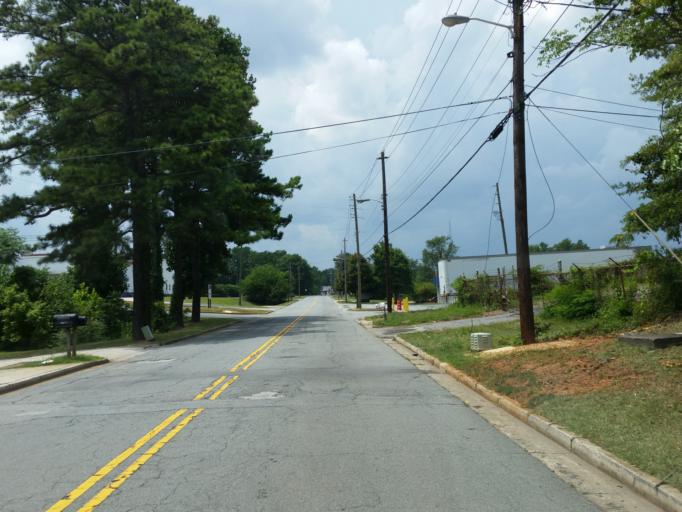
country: US
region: Georgia
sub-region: Cobb County
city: Marietta
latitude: 33.9752
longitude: -84.5386
